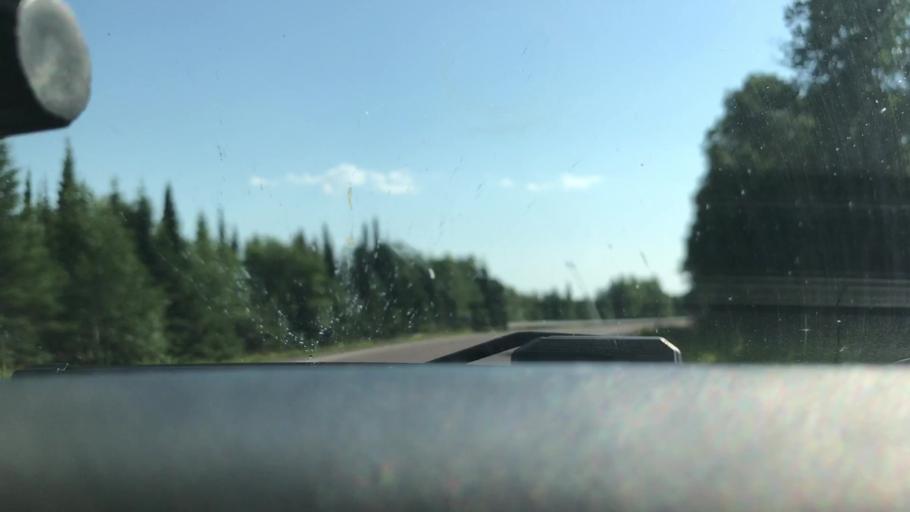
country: US
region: Minnesota
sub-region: Cook County
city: Grand Marais
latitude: 47.8324
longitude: -89.9765
